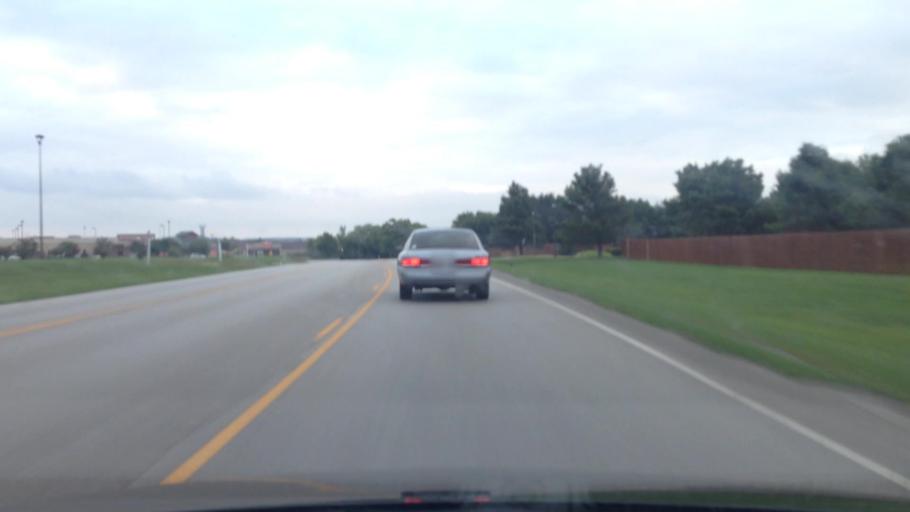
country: US
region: Texas
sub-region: Johnson County
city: Burleson
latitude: 32.5160
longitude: -97.3458
